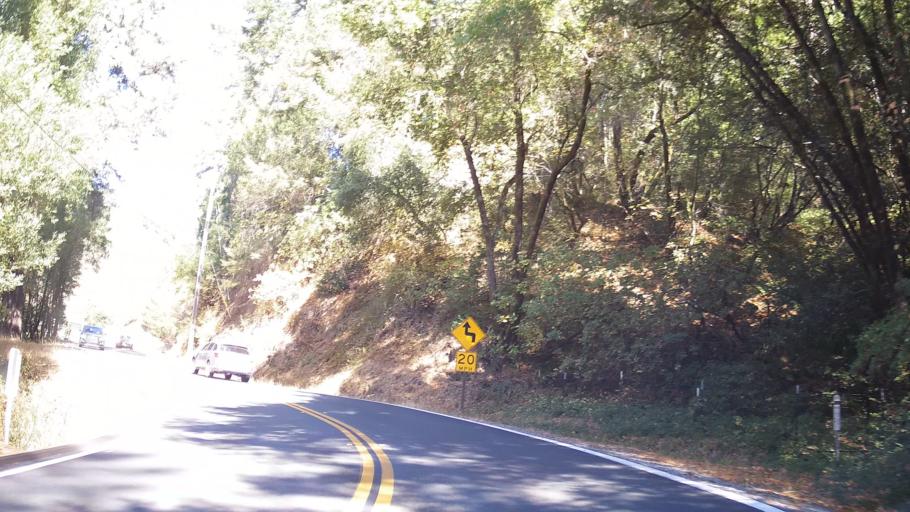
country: US
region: California
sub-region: Marin County
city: Woodacre
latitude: 38.0430
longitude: -122.6357
